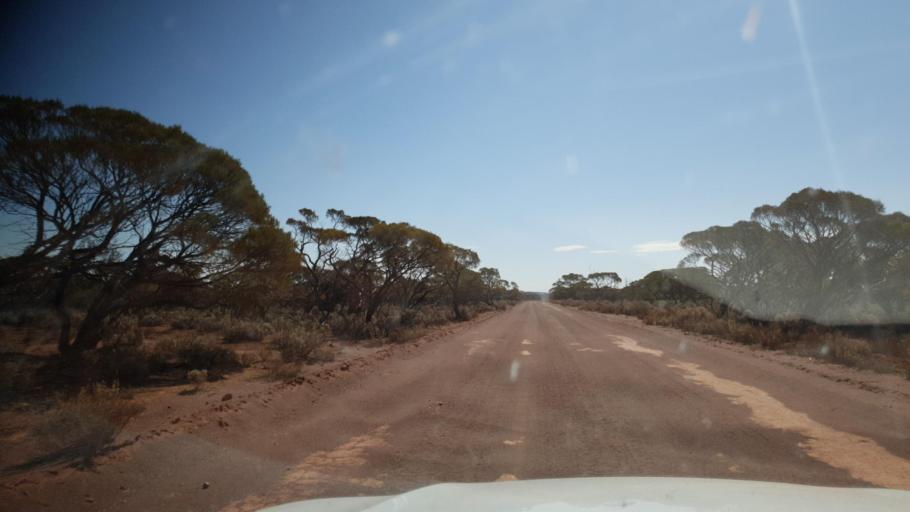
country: AU
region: South Australia
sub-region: Kimba
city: Caralue
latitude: -32.4852
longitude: 136.0538
